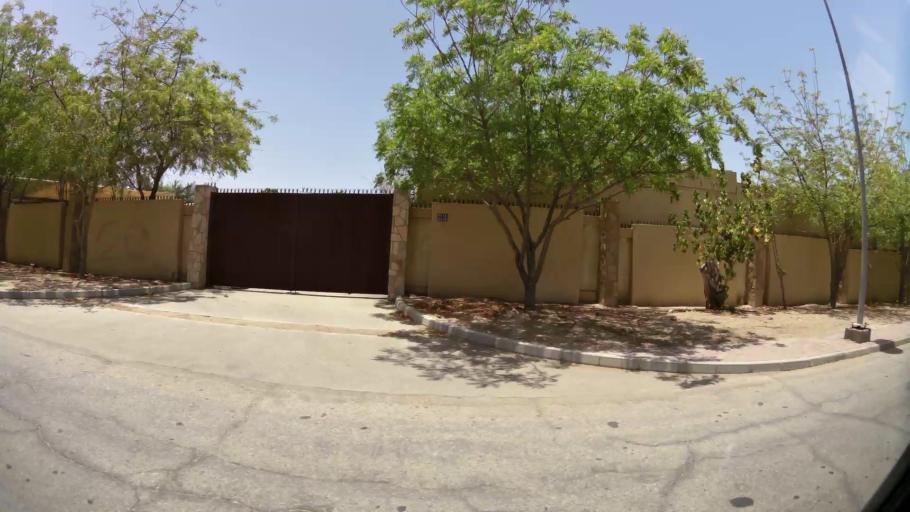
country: OM
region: Muhafazat Masqat
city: Bawshar
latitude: 23.6117
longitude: 58.4810
